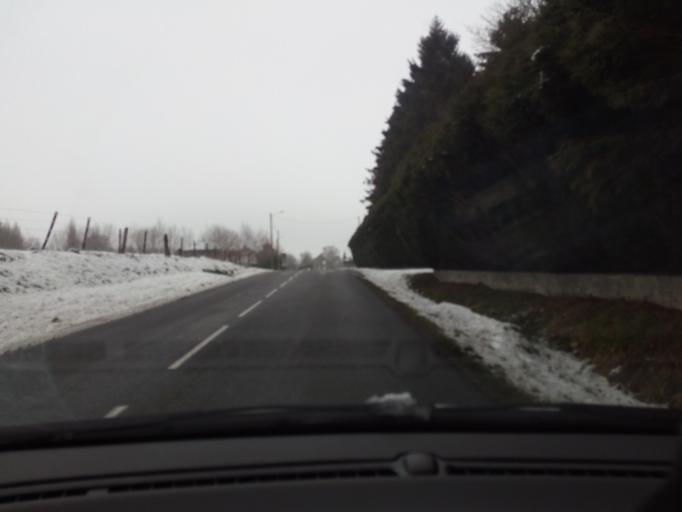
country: FR
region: Nord-Pas-de-Calais
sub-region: Departement du Nord
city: Maubeuge
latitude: 50.2926
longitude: 3.9897
